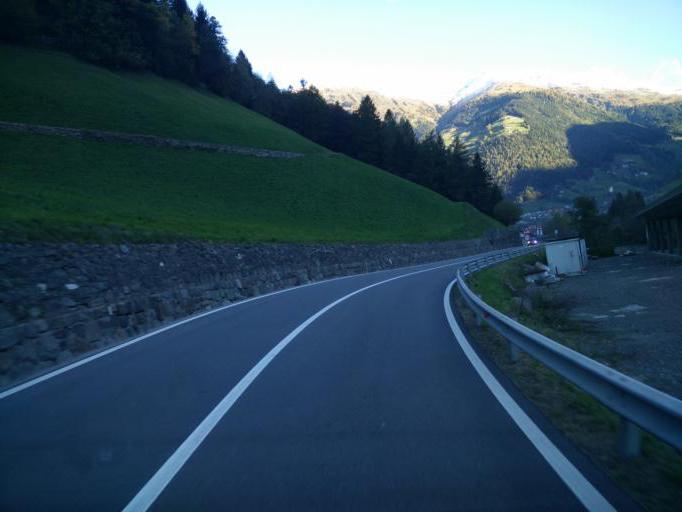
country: IT
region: Trentino-Alto Adige
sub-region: Bolzano
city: San Martino in Passiria
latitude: 46.7962
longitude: 11.2331
